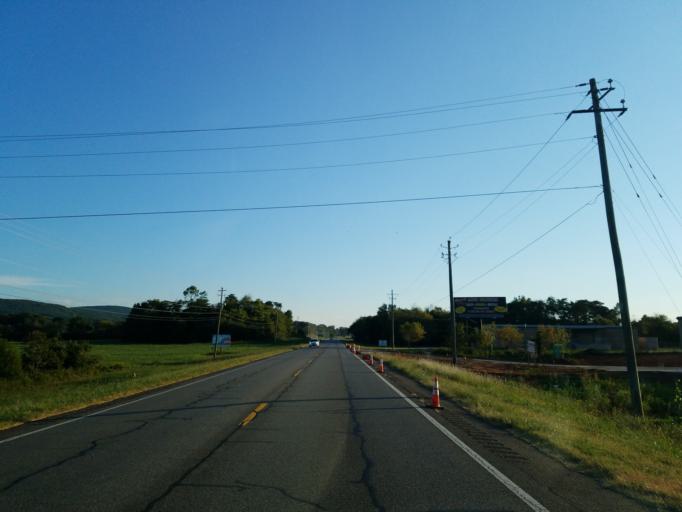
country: US
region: Georgia
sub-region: Bartow County
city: Rydal
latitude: 34.3320
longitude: -84.7160
